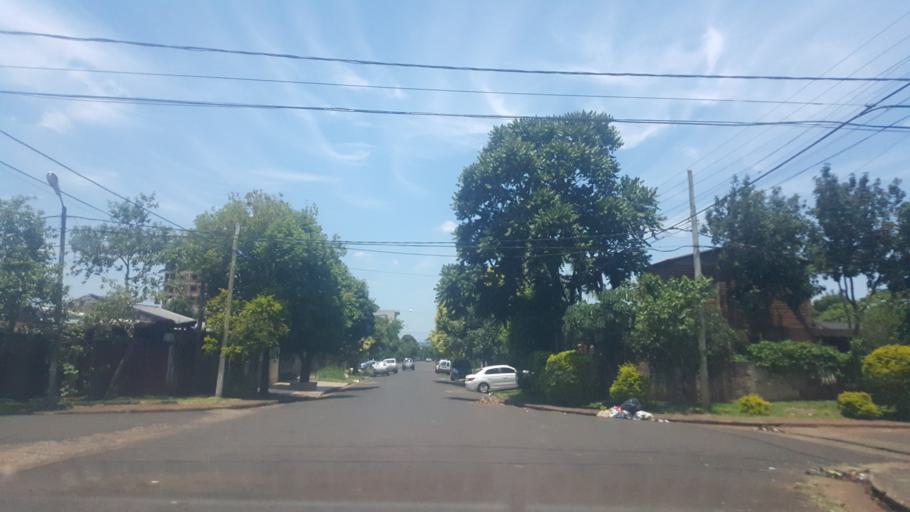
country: AR
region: Misiones
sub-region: Departamento de Capital
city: Posadas
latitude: -27.3884
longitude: -55.9067
